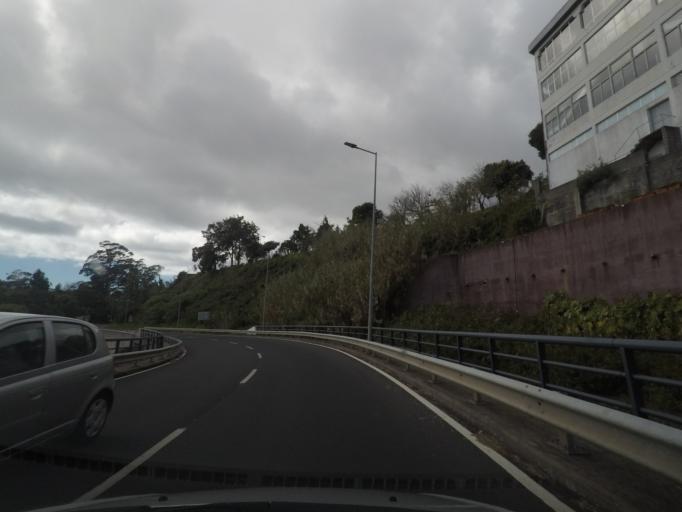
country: PT
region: Madeira
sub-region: Santa Cruz
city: Camacha
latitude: 32.6786
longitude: -16.8442
